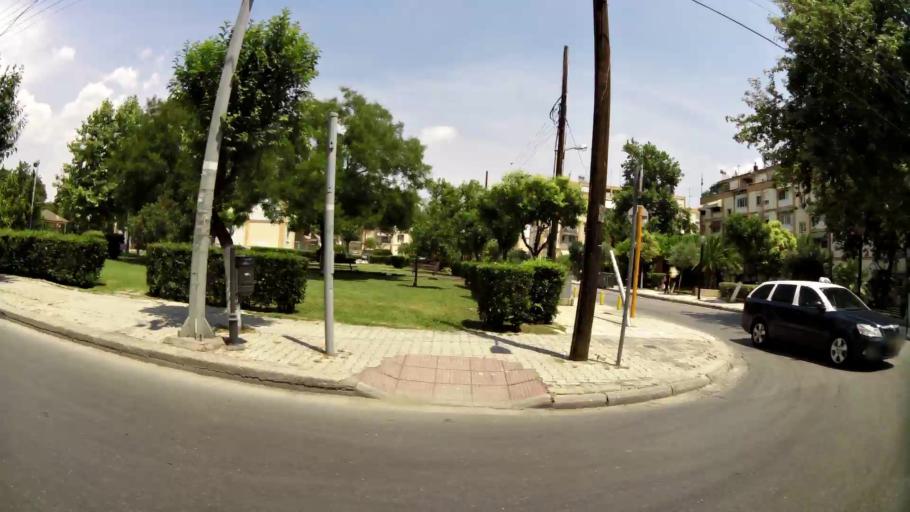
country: GR
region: Central Macedonia
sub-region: Nomos Thessalonikis
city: Ampelokipoi
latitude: 40.6555
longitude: 22.9175
